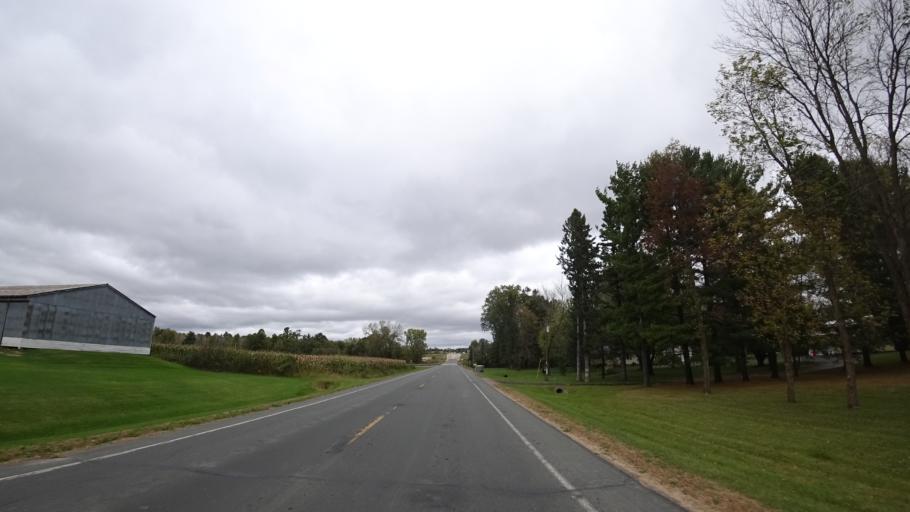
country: US
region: Wisconsin
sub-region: Saint Croix County
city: Woodville
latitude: 44.9286
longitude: -92.2783
